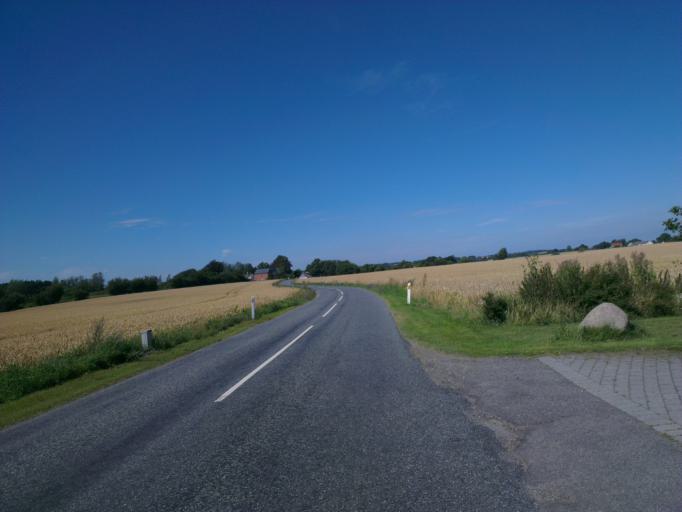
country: DK
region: Capital Region
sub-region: Frederikssund Kommune
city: Frederikssund
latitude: 55.8672
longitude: 12.0904
